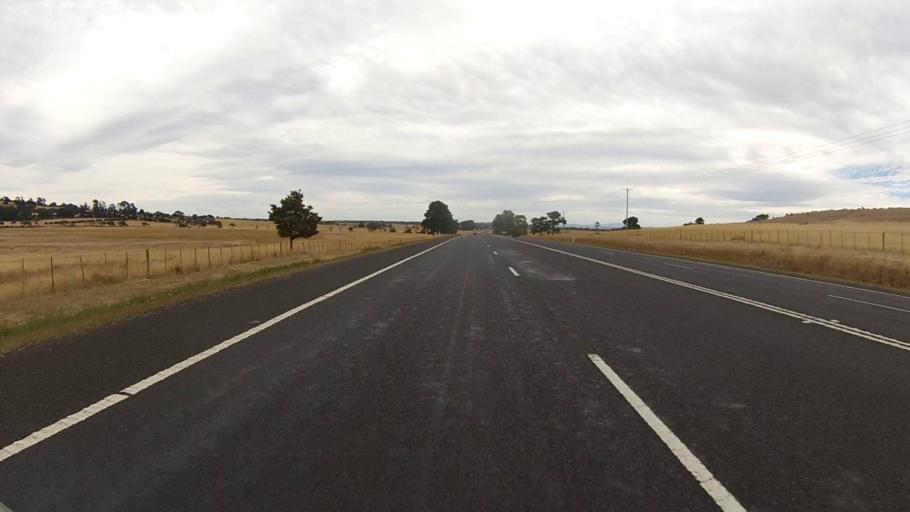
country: AU
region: Tasmania
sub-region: Northern Midlands
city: Evandale
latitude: -41.8708
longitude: 147.4601
